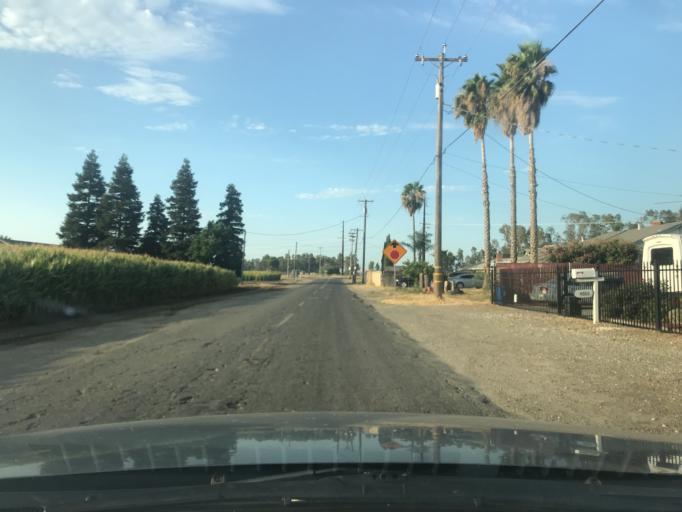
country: US
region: California
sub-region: Merced County
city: Atwater
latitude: 37.3481
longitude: -120.5496
